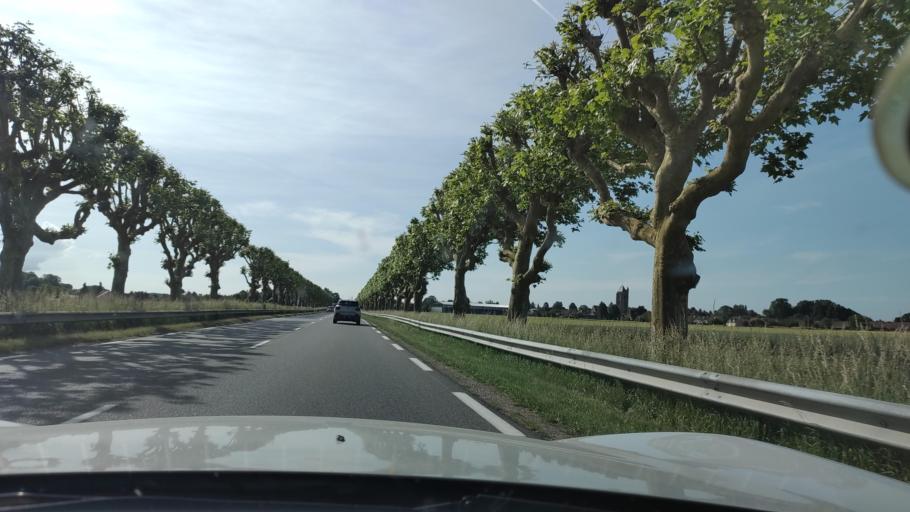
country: FR
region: Ile-de-France
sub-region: Departement de Seine-et-Marne
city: Sourdun
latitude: 48.5428
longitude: 3.3434
